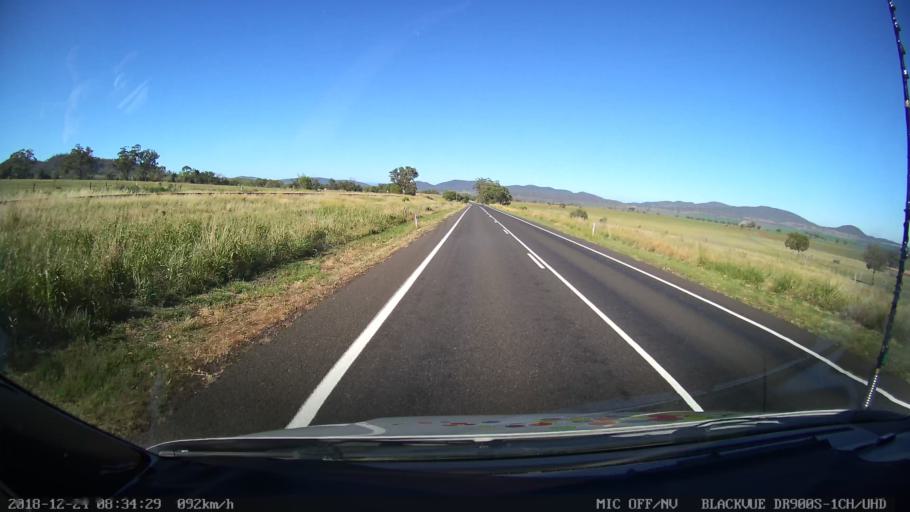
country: AU
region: New South Wales
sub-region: Liverpool Plains
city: Quirindi
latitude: -31.2931
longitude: 150.6704
